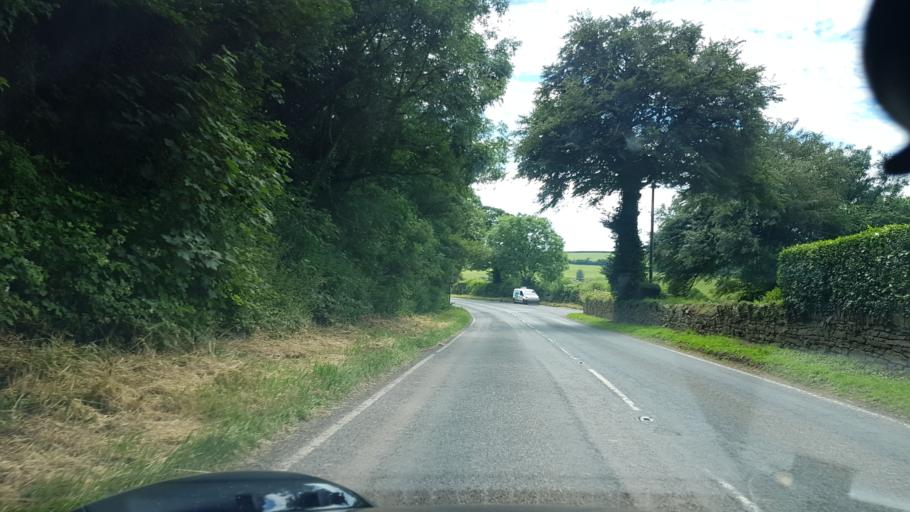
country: GB
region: Wales
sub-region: Carmarthenshire
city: Saint Clears
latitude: 51.7811
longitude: -4.4704
